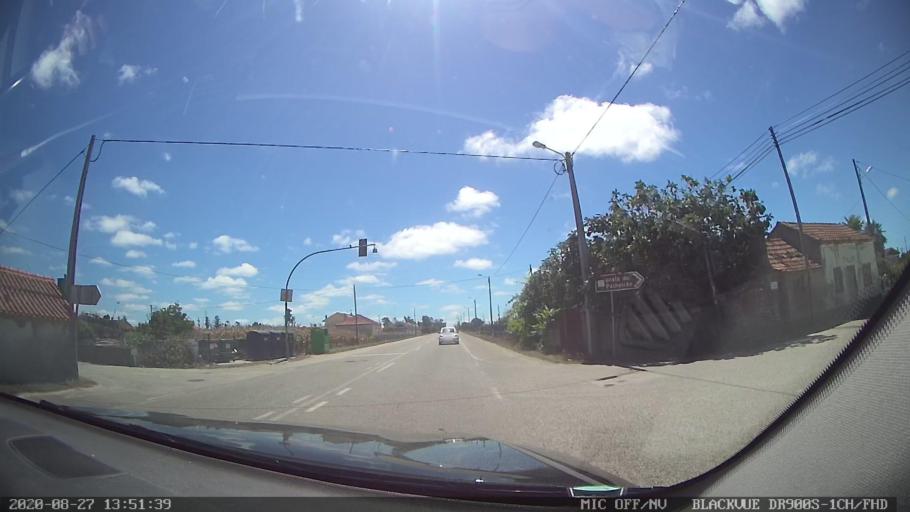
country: PT
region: Coimbra
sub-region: Mira
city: Mira
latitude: 40.3460
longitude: -8.7491
